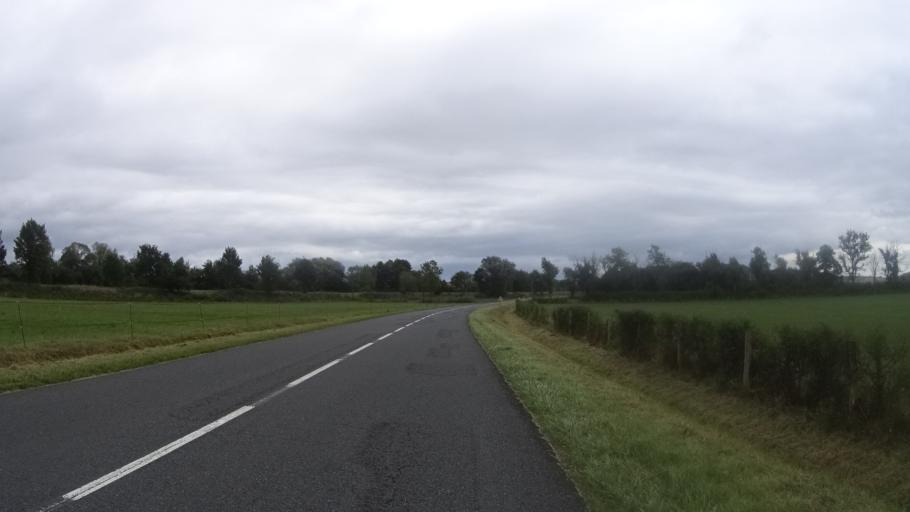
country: FR
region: Lorraine
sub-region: Departement de la Moselle
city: Dieuze
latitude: 48.6891
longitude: 6.6774
